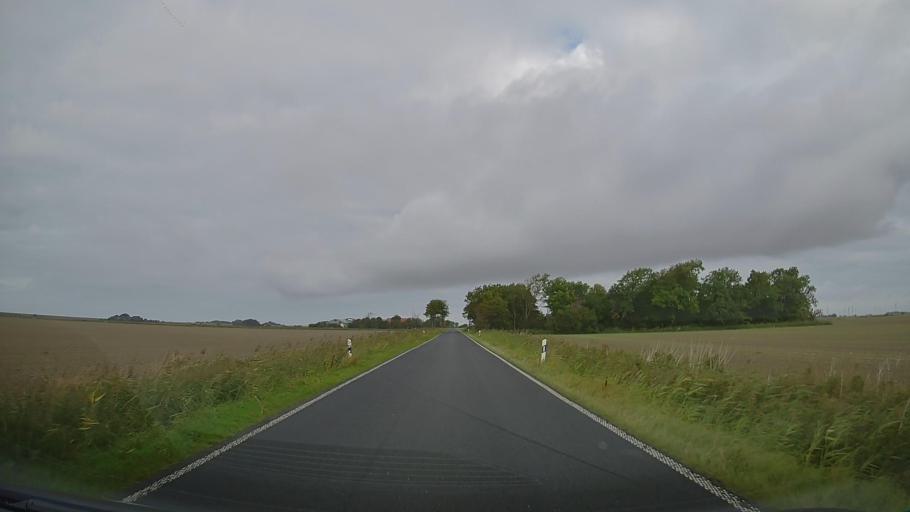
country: DE
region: Schleswig-Holstein
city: Galmsbull
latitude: 54.7519
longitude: 8.7297
